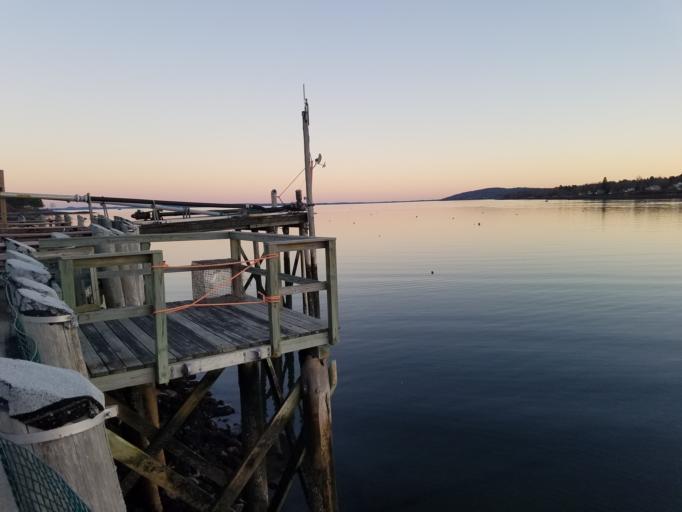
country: US
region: Maine
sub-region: Waldo County
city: Belfast
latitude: 44.4294
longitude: -69.0083
